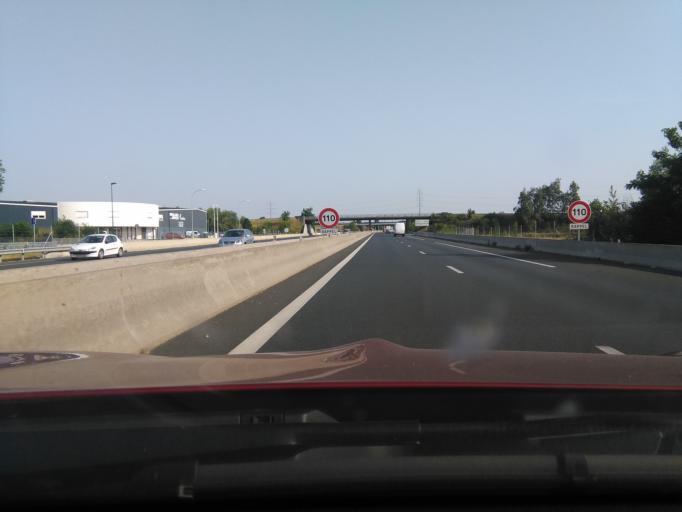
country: FR
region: Rhone-Alpes
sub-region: Departement du Rhone
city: Cailloux-sur-Fontaines
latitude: 45.8649
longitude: 4.9061
